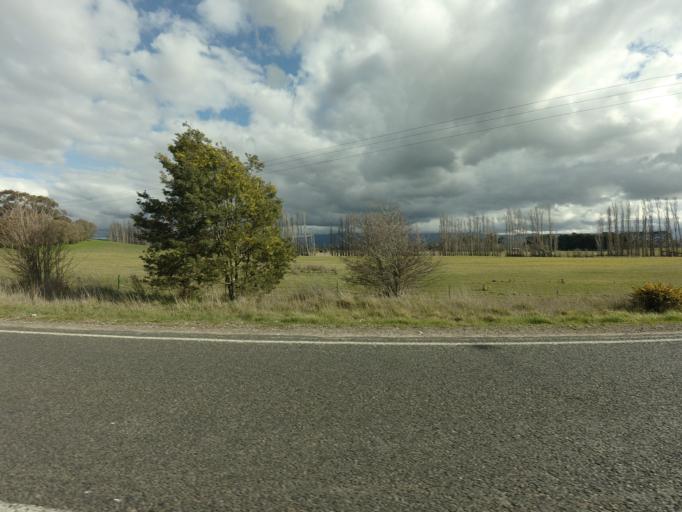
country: AU
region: Tasmania
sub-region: Northern Midlands
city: Longford
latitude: -41.7168
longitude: 147.0893
